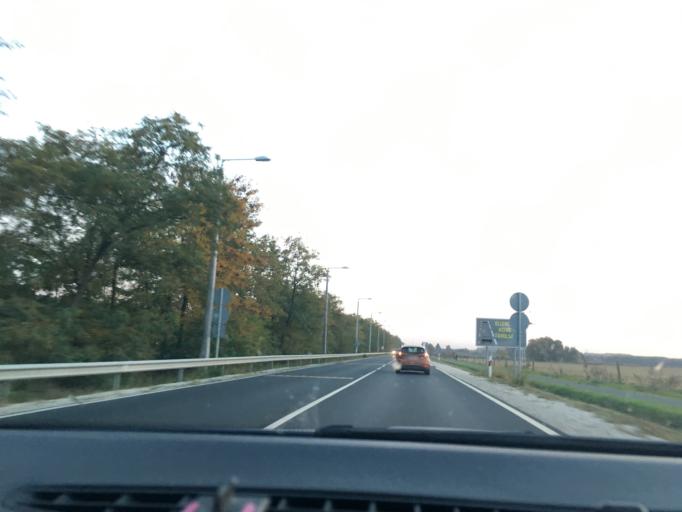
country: HU
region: Hajdu-Bihar
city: Hajduhadhaz
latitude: 47.6353
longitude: 21.6592
